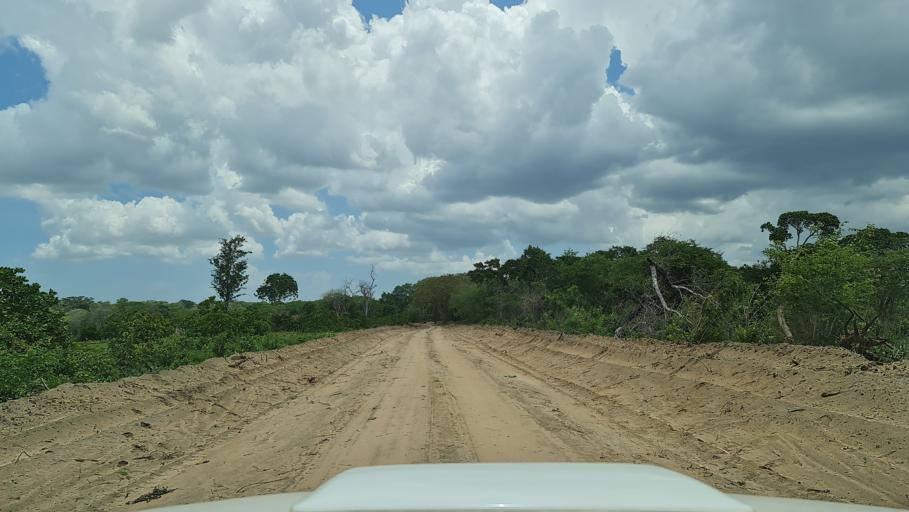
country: MZ
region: Nampula
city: Ilha de Mocambique
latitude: -15.2474
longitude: 40.3680
